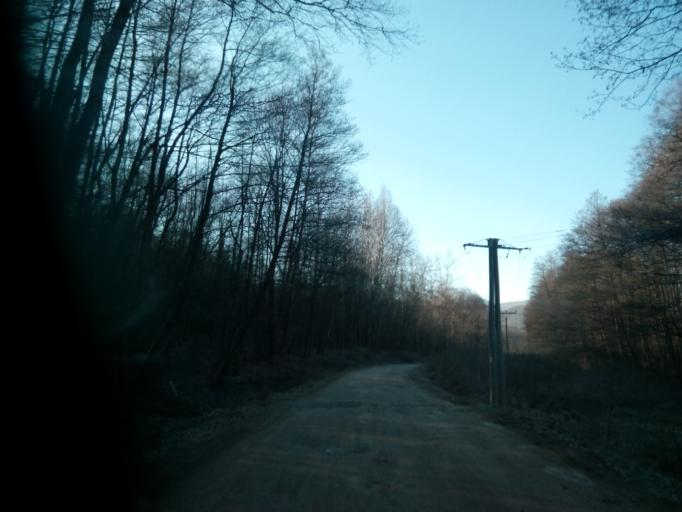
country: SK
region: Kosicky
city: Medzev
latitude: 48.6856
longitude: 20.9061
